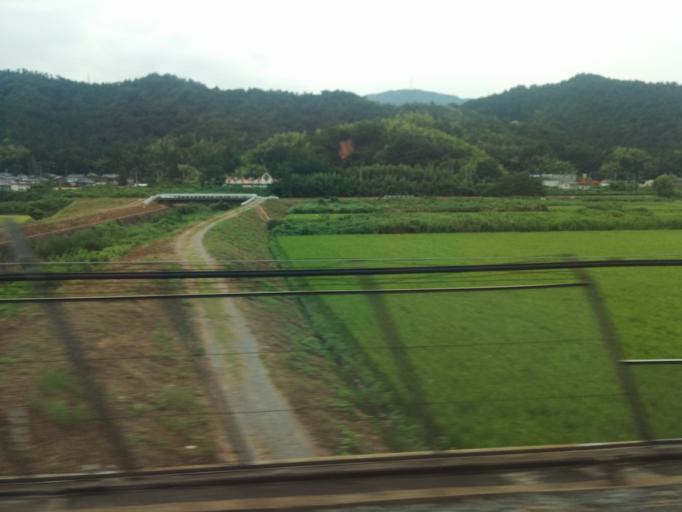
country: JP
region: Shiga Prefecture
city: Hikone
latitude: 35.2973
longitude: 136.2829
